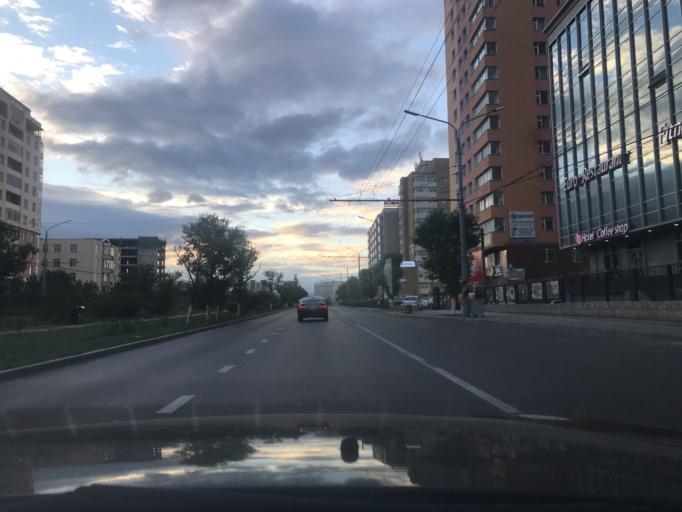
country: MN
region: Ulaanbaatar
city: Ulaanbaatar
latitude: 47.9167
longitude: 106.9605
